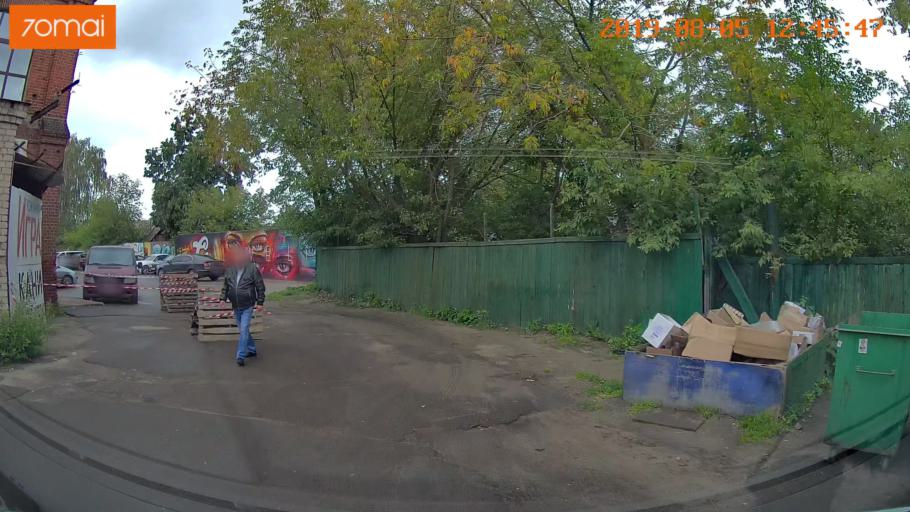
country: RU
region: Ivanovo
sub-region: Gorod Ivanovo
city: Ivanovo
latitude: 56.9870
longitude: 40.9769
